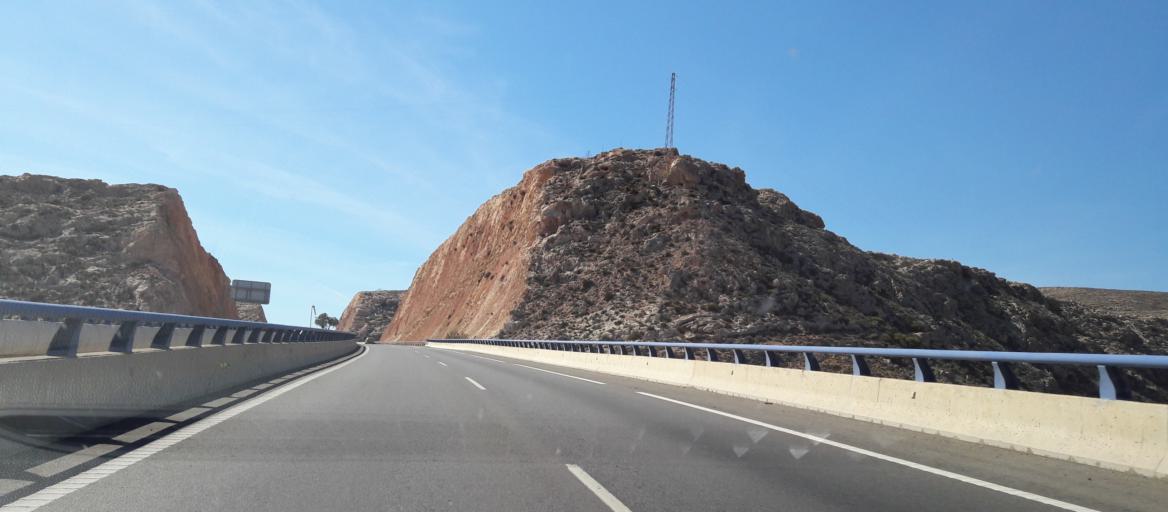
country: ES
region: Andalusia
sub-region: Provincia de Almeria
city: Almeria
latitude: 36.8451
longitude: -2.4835
